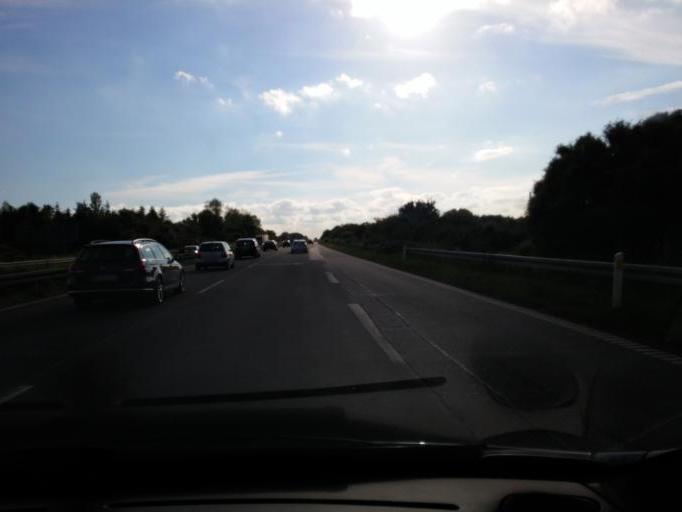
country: DK
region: Zealand
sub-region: Slagelse Kommune
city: Forlev
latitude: 55.3625
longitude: 11.2234
